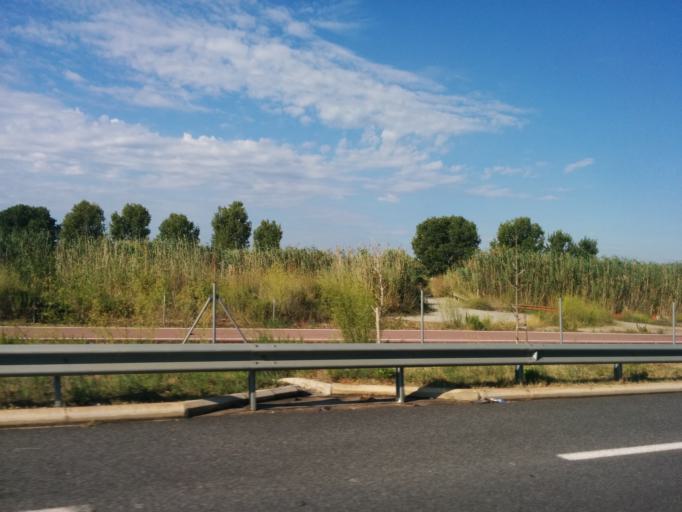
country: ES
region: Catalonia
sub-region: Provincia de Barcelona
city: El Prat de Llobregat
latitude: 41.2903
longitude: 2.0612
